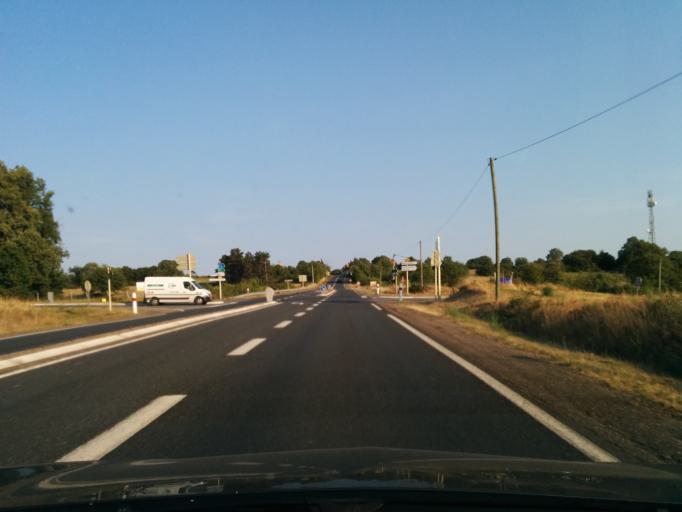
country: FR
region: Midi-Pyrenees
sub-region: Departement du Lot
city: Le Vigan
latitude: 44.6185
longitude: 1.4922
